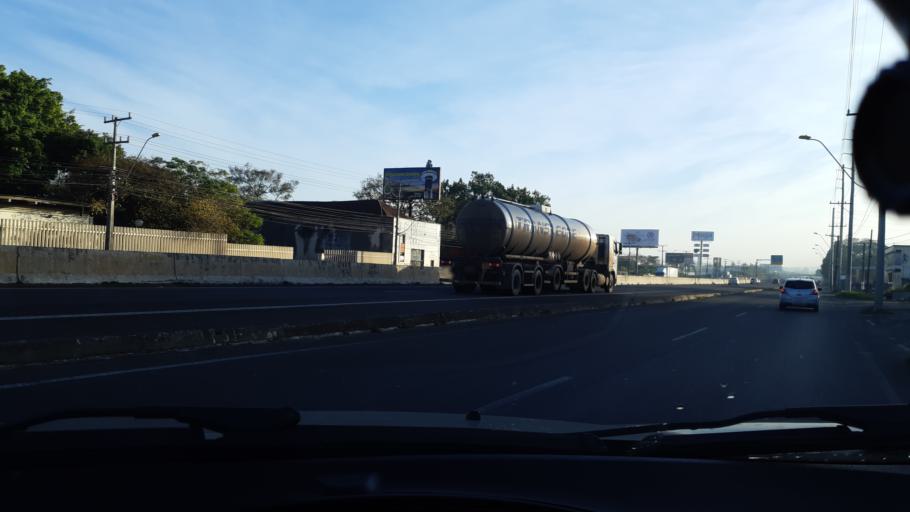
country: BR
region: Rio Grande do Sul
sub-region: Esteio
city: Esteio
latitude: -29.8402
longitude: -51.1761
